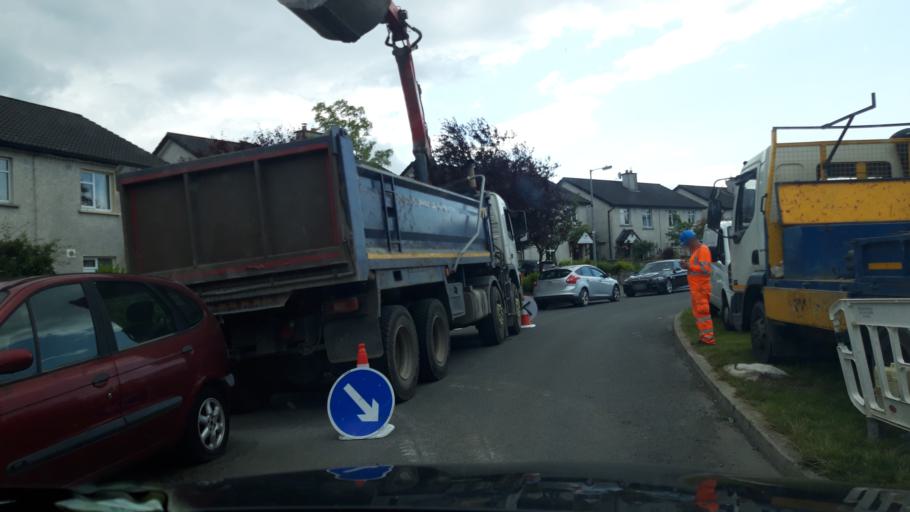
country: IE
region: Leinster
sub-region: Wicklow
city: Blessington
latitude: 53.1757
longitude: -6.5322
